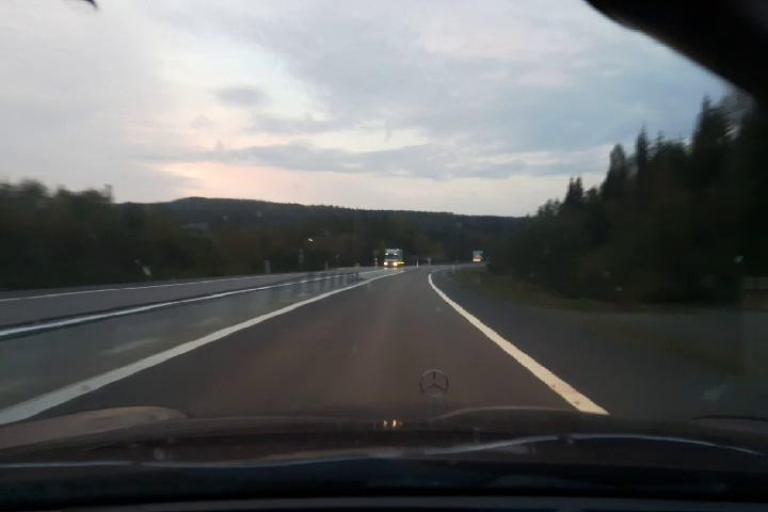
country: SE
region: Vaesternorrland
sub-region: Kramfors Kommun
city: Nordingra
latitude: 62.9512
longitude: 18.0957
